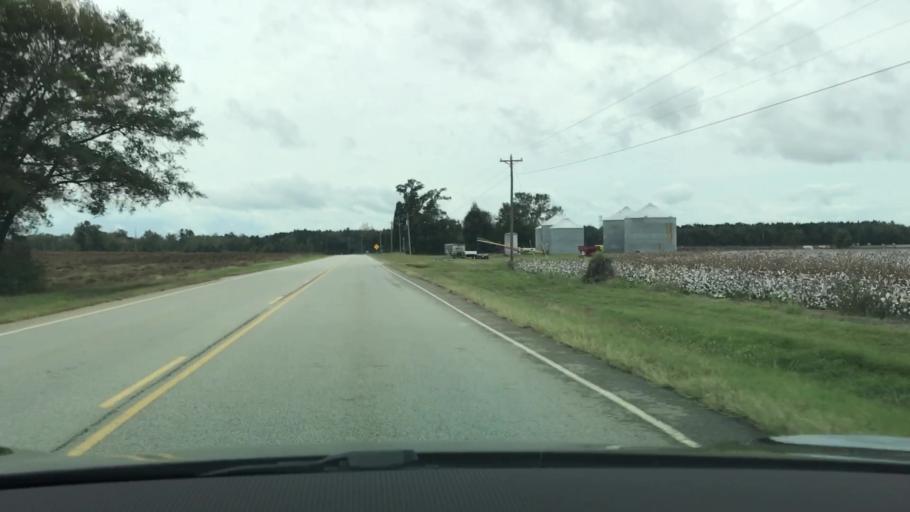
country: US
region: Georgia
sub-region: Jefferson County
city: Wrens
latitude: 33.1460
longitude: -82.4570
